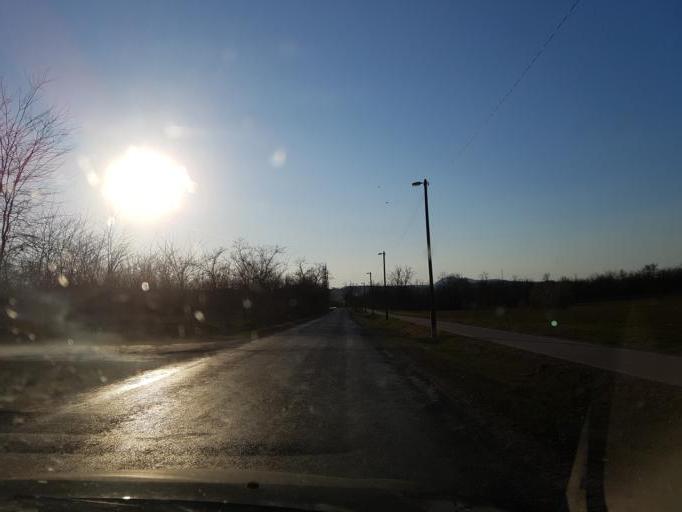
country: HU
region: Komarom-Esztergom
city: Piliscsev
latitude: 47.6732
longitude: 18.7964
